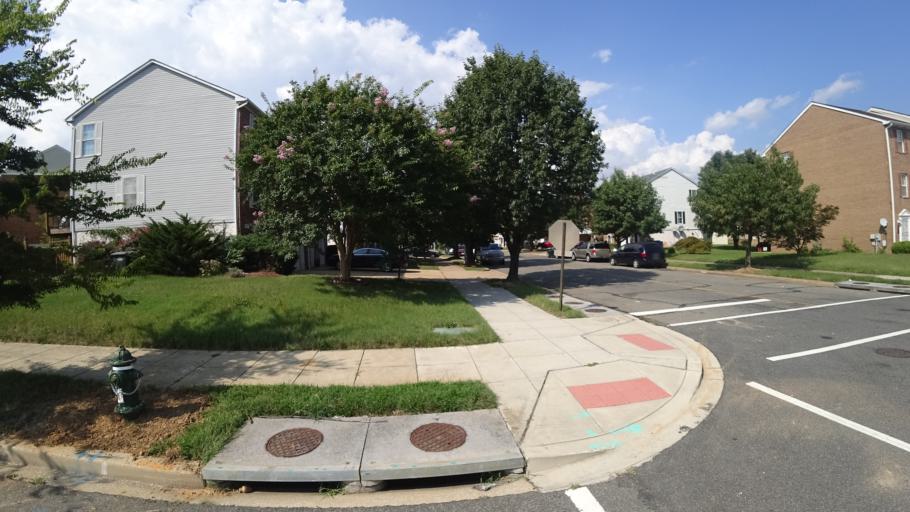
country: US
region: Maryland
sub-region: Prince George's County
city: Hillcrest Heights
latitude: 38.8519
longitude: -76.9681
